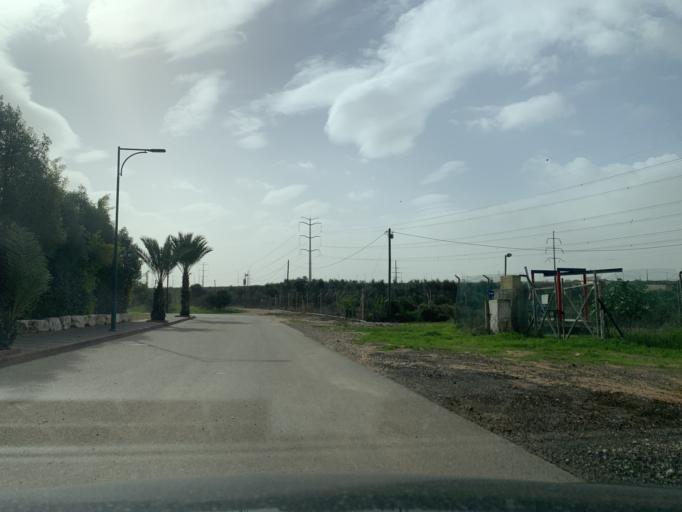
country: IL
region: Central District
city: Jaljulya
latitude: 32.1578
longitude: 34.9386
